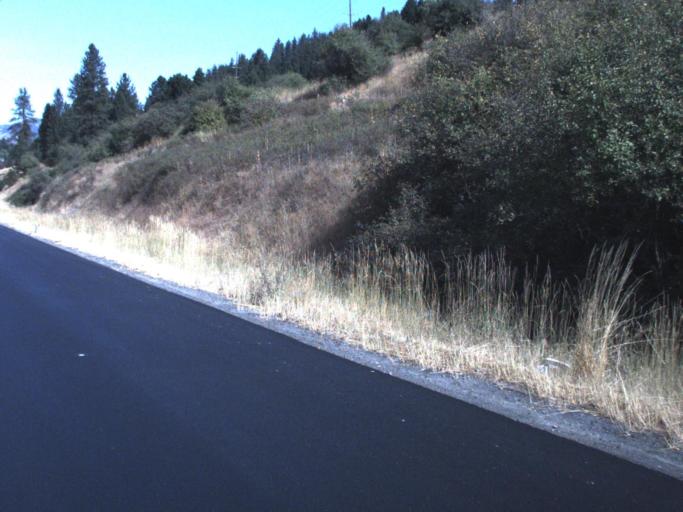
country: US
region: Washington
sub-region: Stevens County
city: Colville
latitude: 48.5075
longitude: -117.9019
